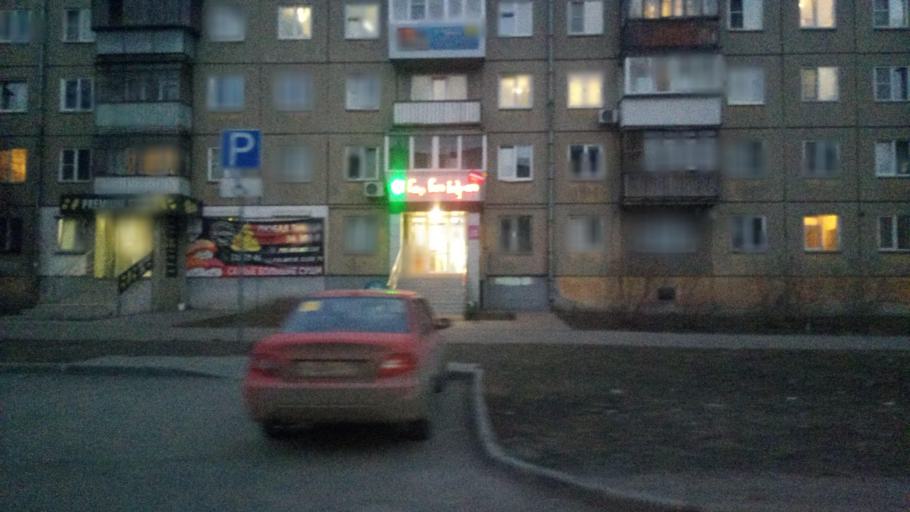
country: RU
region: Chelyabinsk
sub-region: Gorod Chelyabinsk
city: Chelyabinsk
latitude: 55.1715
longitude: 61.4632
